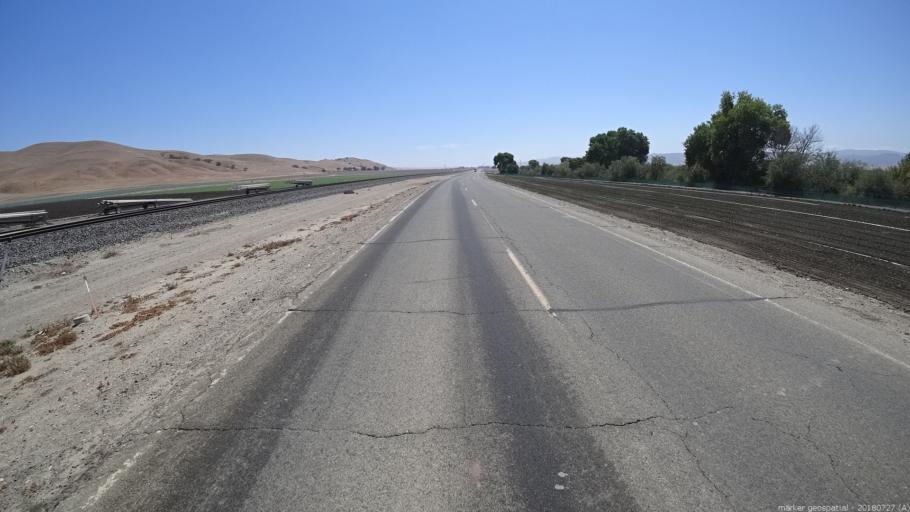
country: US
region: California
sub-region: Monterey County
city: King City
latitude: 36.0574
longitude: -120.9237
